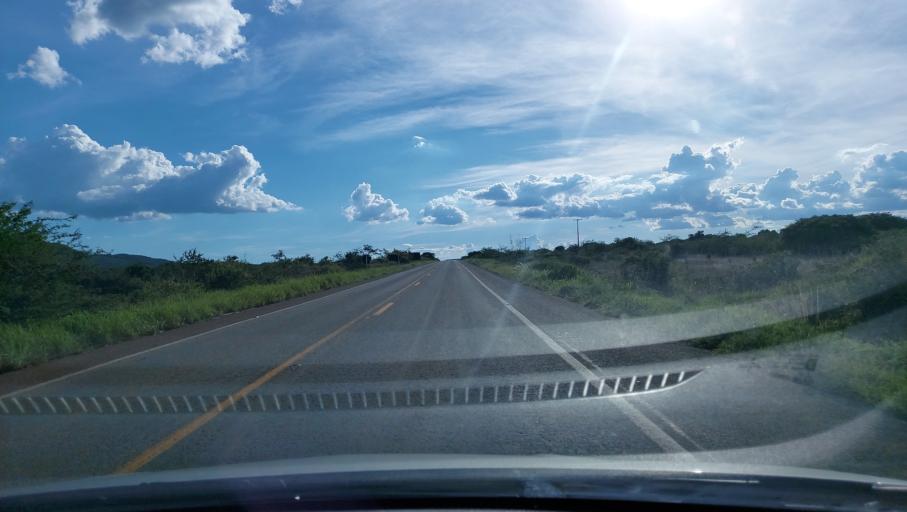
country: BR
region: Bahia
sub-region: Seabra
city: Seabra
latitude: -12.4271
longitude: -42.1141
